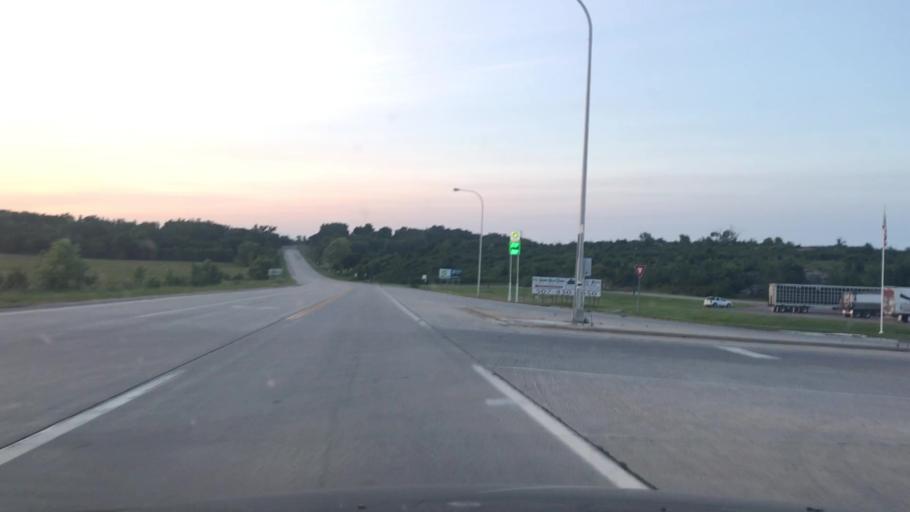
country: US
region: Minnesota
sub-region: Redwood County
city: Redwood Falls
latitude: 44.5490
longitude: -94.9949
